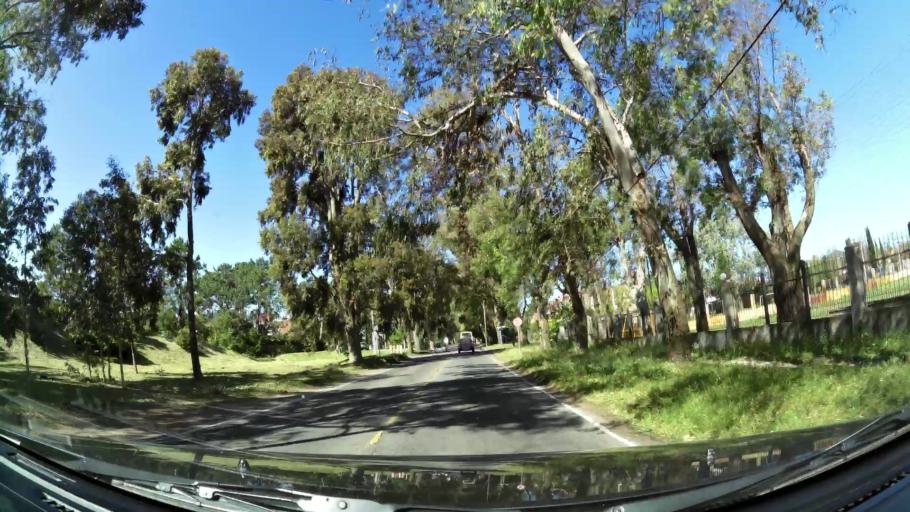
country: UY
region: Canelones
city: Barra de Carrasco
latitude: -34.8801
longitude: -56.0409
